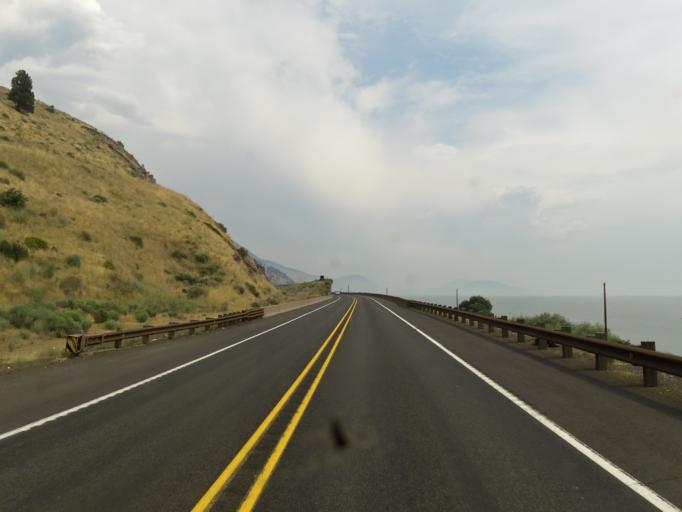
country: US
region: Oregon
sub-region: Klamath County
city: Klamath Falls
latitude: 42.4358
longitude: -121.8653
